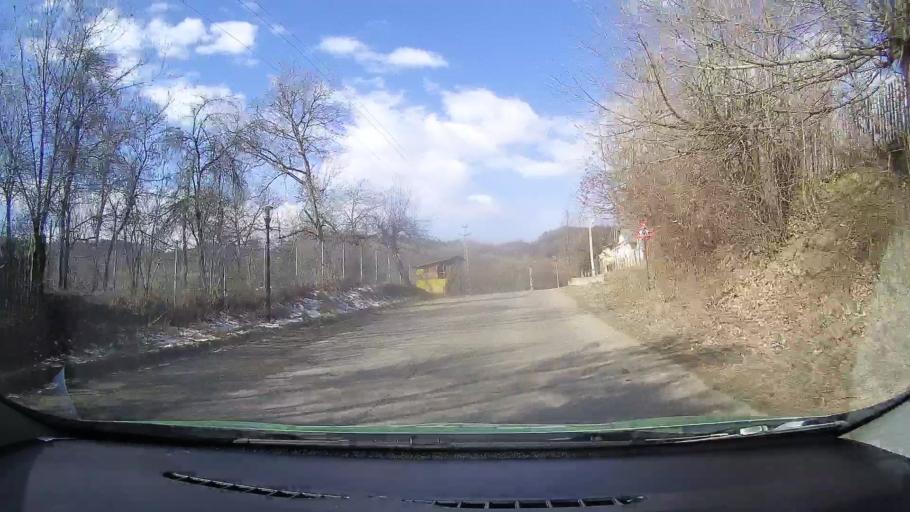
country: RO
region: Dambovita
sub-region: Comuna Varfuri
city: Varfuri
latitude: 45.0900
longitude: 25.4836
